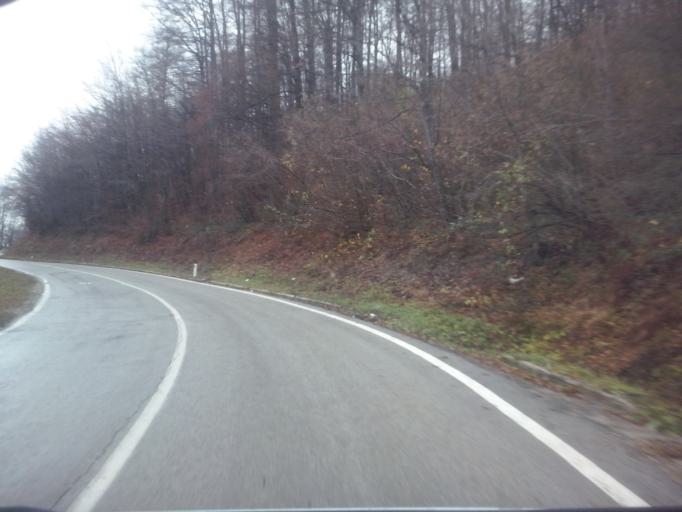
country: RS
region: Central Serbia
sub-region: Moravicki Okrug
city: Ivanjica
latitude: 43.5263
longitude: 20.3299
